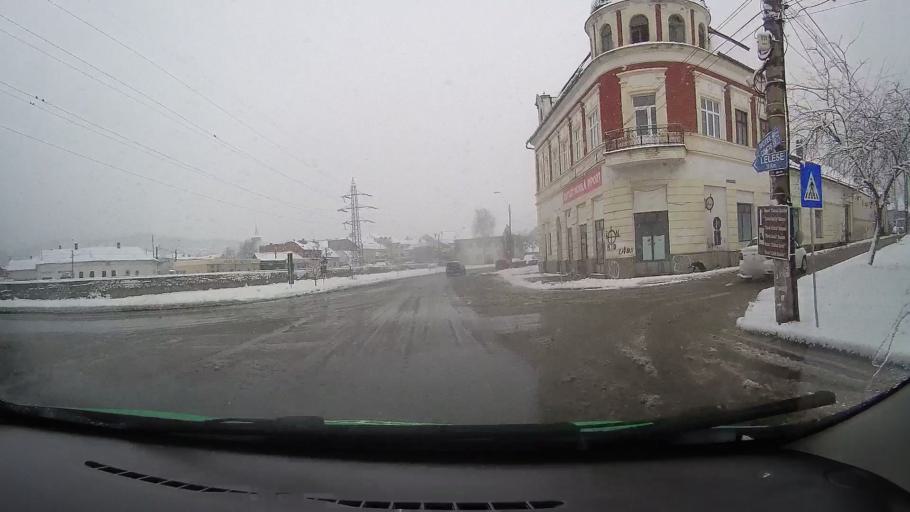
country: RO
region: Hunedoara
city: Hunedoara
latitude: 45.7509
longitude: 22.8937
